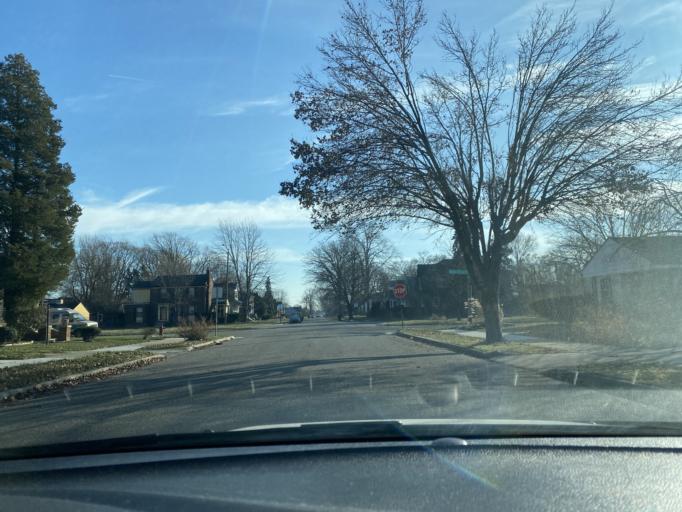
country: US
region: Michigan
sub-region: Wayne County
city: Grosse Pointe Park
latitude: 42.4042
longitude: -82.9534
